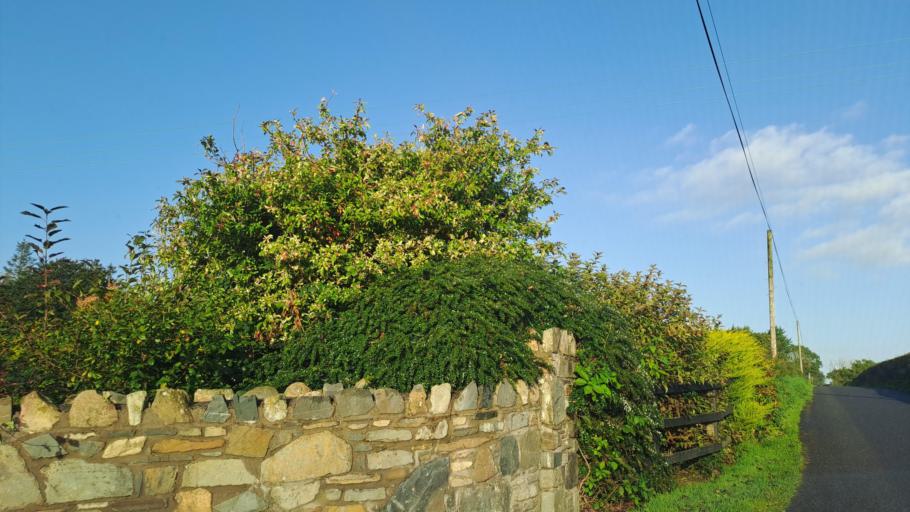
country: IE
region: Ulster
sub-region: County Monaghan
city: Castleblayney
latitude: 54.0601
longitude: -6.8192
